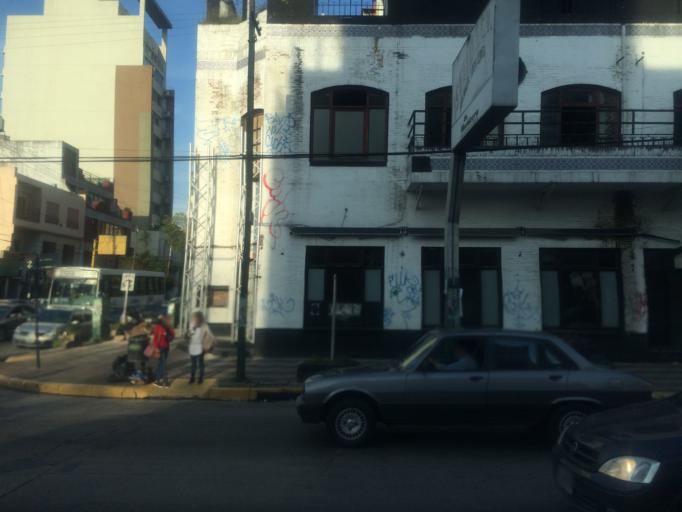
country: AR
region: Buenos Aires
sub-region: Partido de Lomas de Zamora
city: Lomas de Zamora
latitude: -34.7445
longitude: -58.3934
